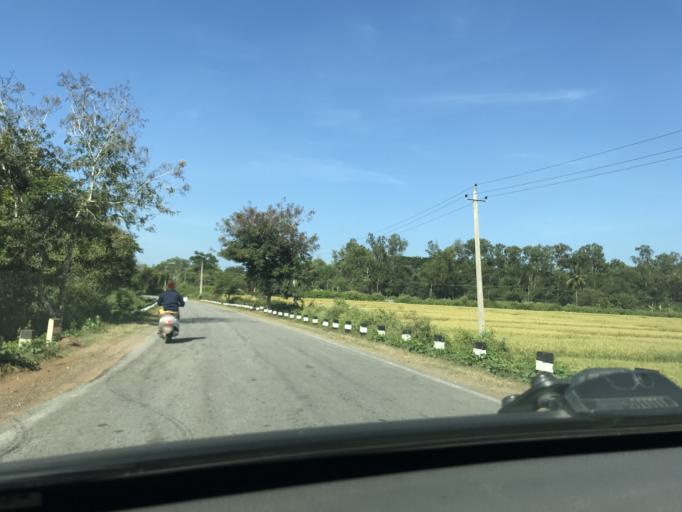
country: IN
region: Karnataka
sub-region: Mysore
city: Heggadadevankote
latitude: 12.1248
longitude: 76.4275
